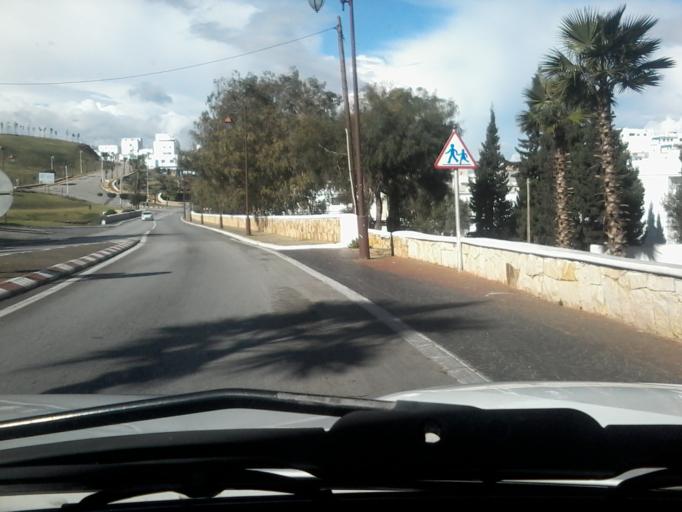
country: MA
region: Tanger-Tetouan
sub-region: Tetouan
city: Martil
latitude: 35.6757
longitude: -5.3221
